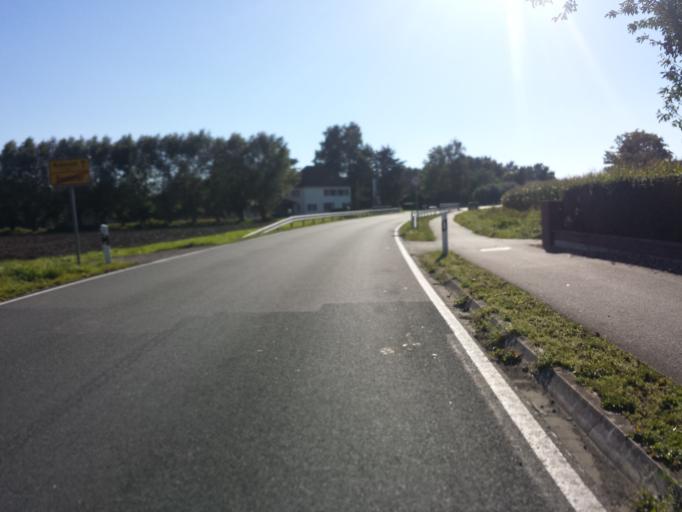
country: DE
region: North Rhine-Westphalia
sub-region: Regierungsbezirk Detmold
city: Langenberg
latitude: 51.7439
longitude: 8.3201
